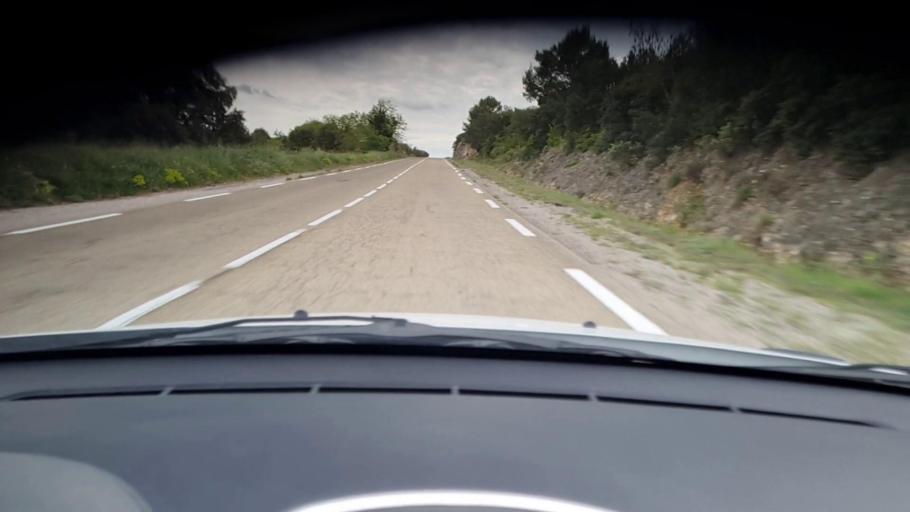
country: FR
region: Languedoc-Roussillon
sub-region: Departement du Gard
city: Poulx
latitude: 43.9105
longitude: 4.3896
